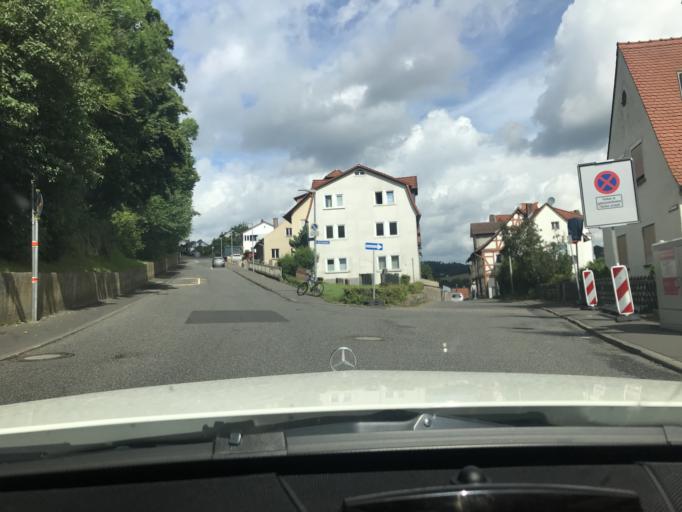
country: DE
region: Hesse
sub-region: Regierungsbezirk Kassel
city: Bad Hersfeld
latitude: 50.8706
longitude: 9.7038
